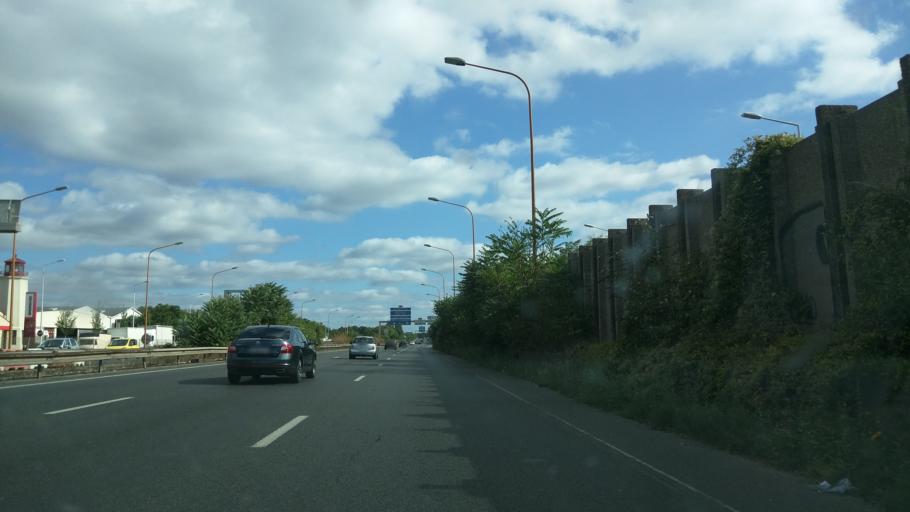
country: FR
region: Ile-de-France
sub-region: Departement du Val-d'Oise
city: Bezons
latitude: 48.9132
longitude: 2.2185
